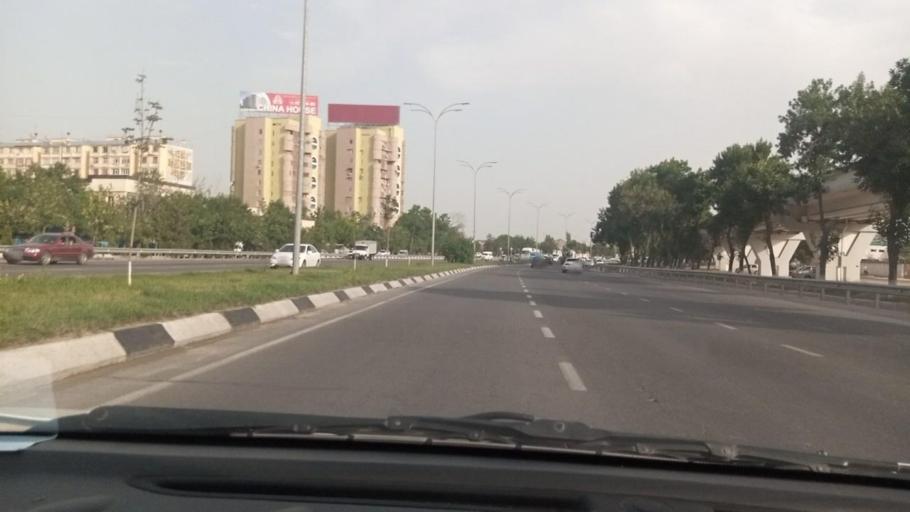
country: UZ
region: Toshkent Shahri
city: Bektemir
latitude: 41.2903
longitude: 69.3583
